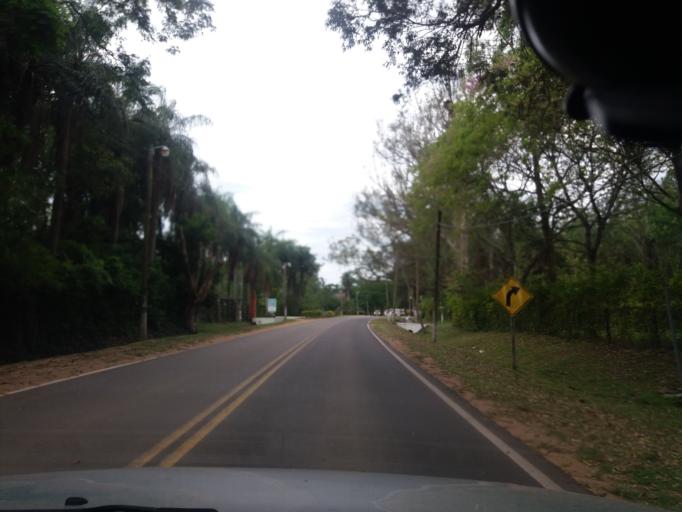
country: AR
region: Corrientes
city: San Luis del Palmar
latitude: -27.4599
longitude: -58.6638
